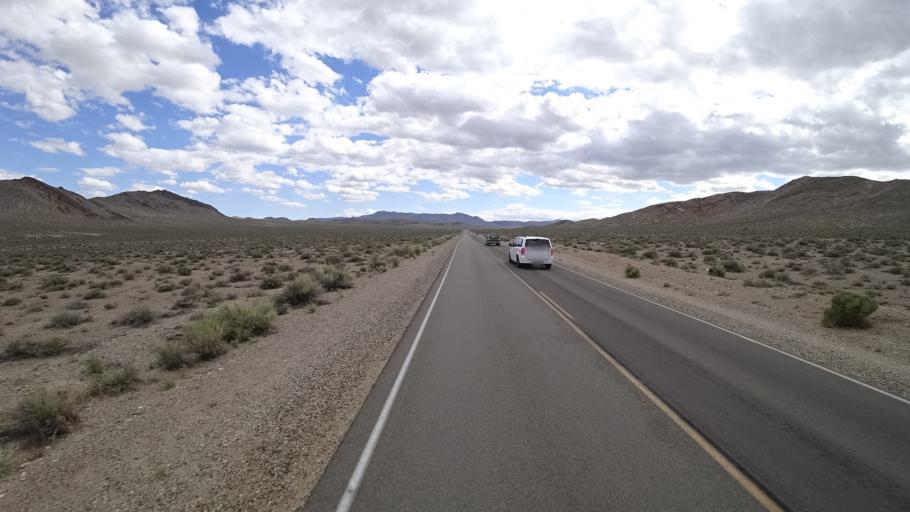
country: US
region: California
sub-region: Inyo County
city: Lone Pine
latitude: 36.3371
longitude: -117.6504
